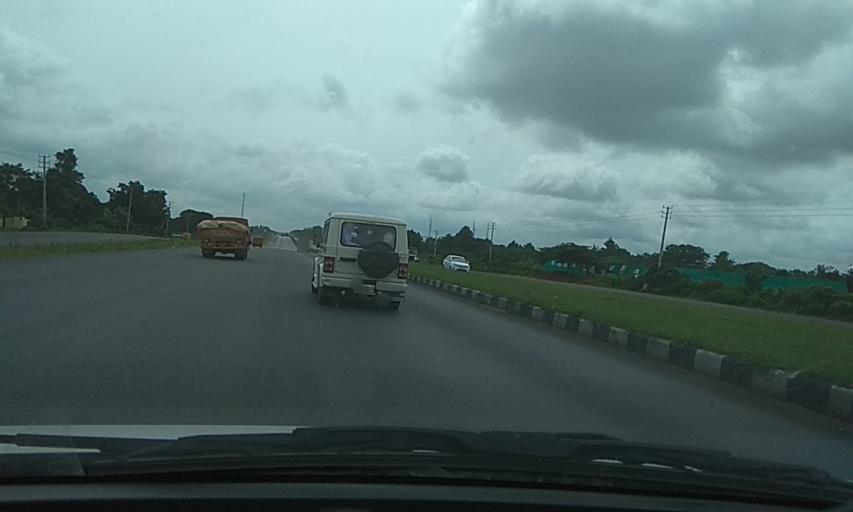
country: IN
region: Karnataka
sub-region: Davanagere
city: Mayakonda
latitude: 14.3962
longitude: 76.0329
